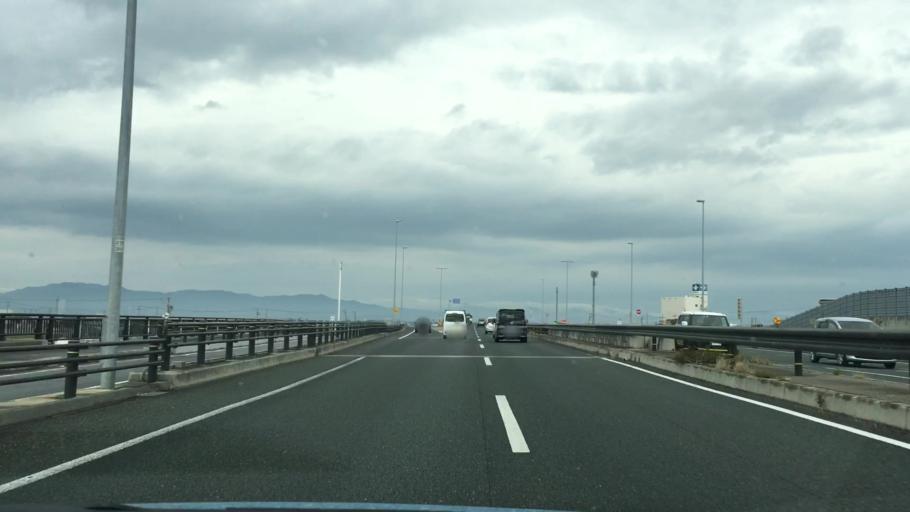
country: JP
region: Aichi
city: Kozakai-cho
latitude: 34.7578
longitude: 137.3336
